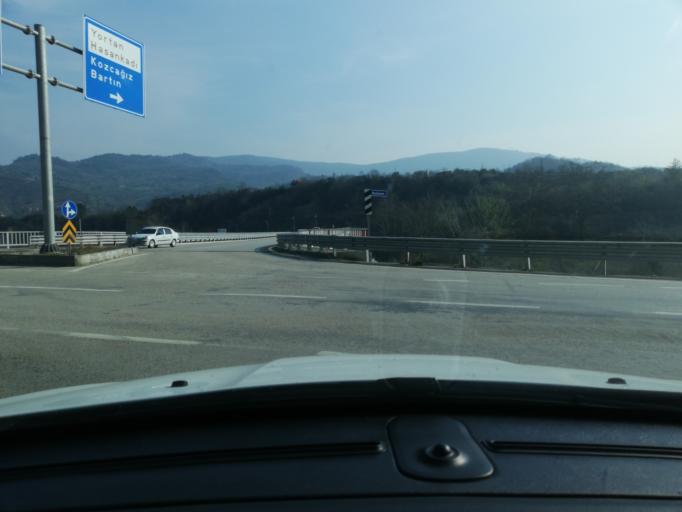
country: TR
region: Karabuk
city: Yenice
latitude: 41.2059
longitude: 32.3656
